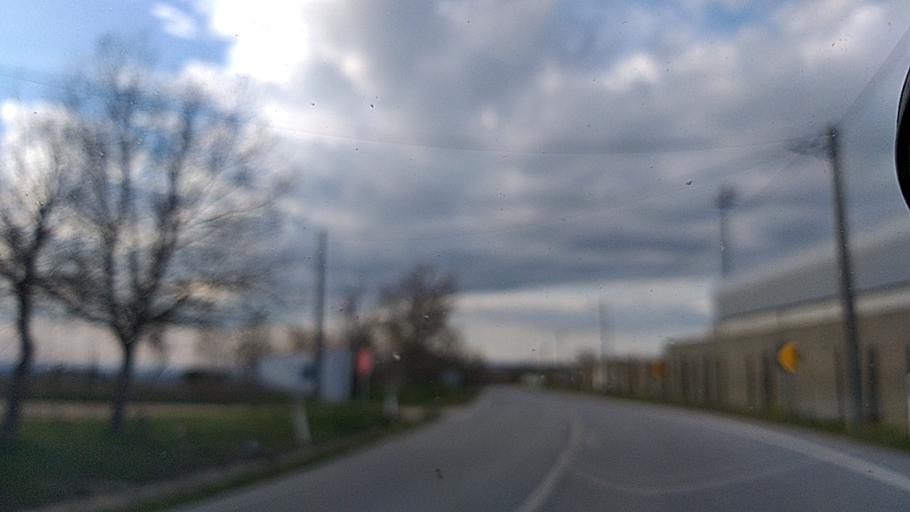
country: ES
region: Castille and Leon
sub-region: Provincia de Salamanca
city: Aldea del Obispo
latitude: 40.7123
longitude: -6.8985
